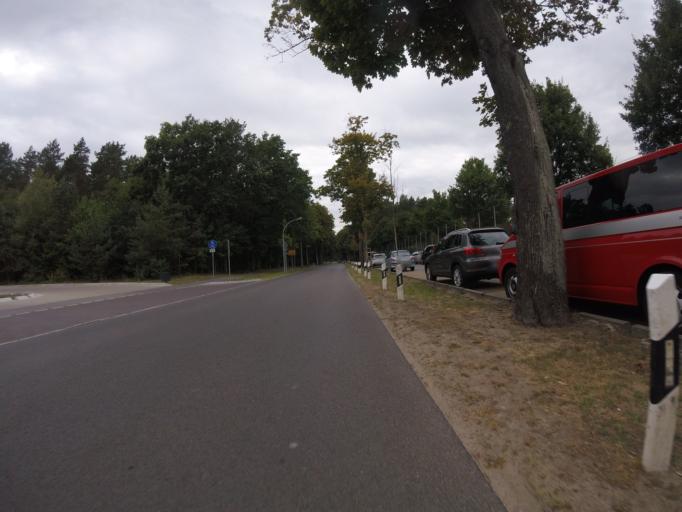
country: DE
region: Brandenburg
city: Birkenwerder
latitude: 52.7154
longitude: 13.2675
